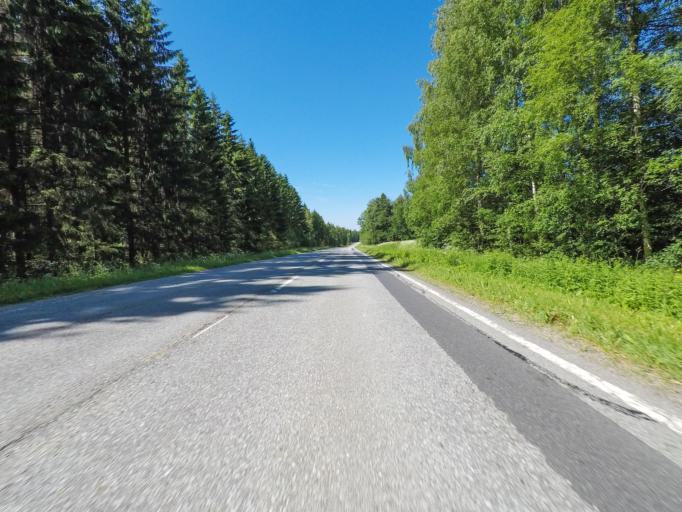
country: FI
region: Southern Savonia
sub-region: Savonlinna
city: Rantasalmi
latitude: 61.9802
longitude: 28.4958
